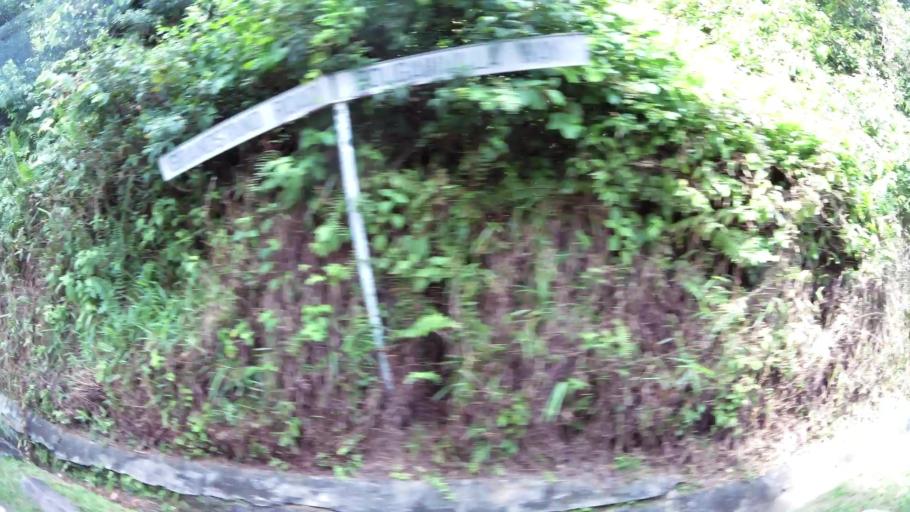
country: SG
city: Singapore
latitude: 1.3396
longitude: 103.7927
